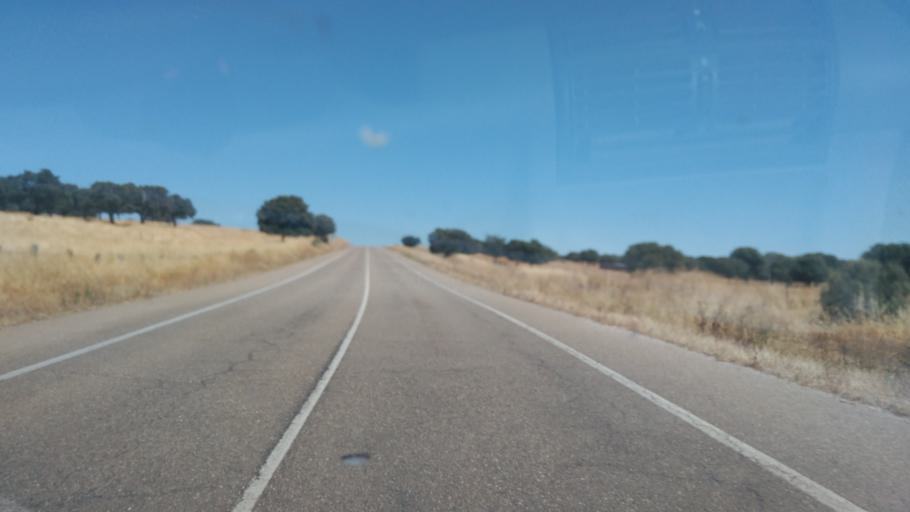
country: ES
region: Castille and Leon
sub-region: Provincia de Salamanca
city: Miranda de Azan
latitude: 40.8727
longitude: -5.7524
